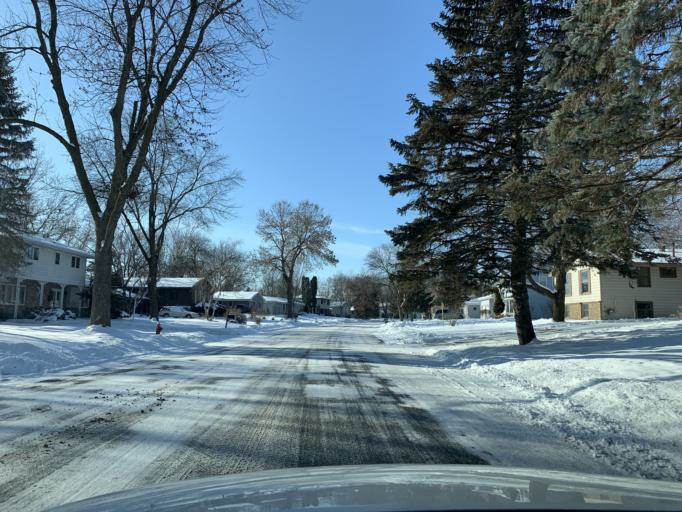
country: US
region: Minnesota
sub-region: Scott County
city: Savage
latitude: 44.8236
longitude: -93.3419
